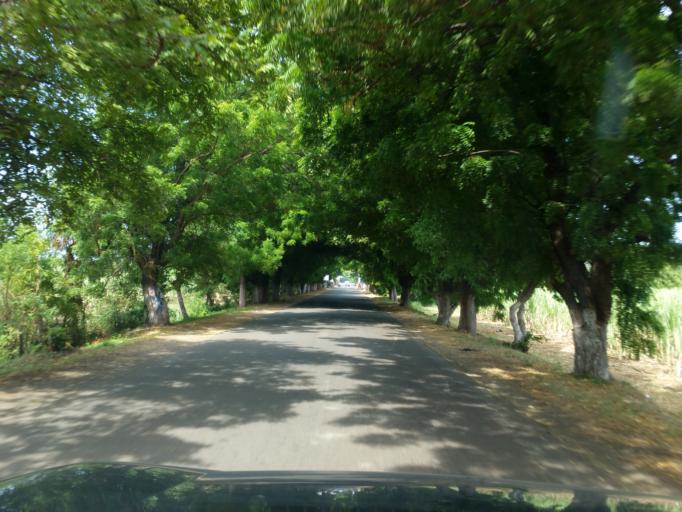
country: NI
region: Managua
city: Masachapa
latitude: 11.7876
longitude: -86.5095
